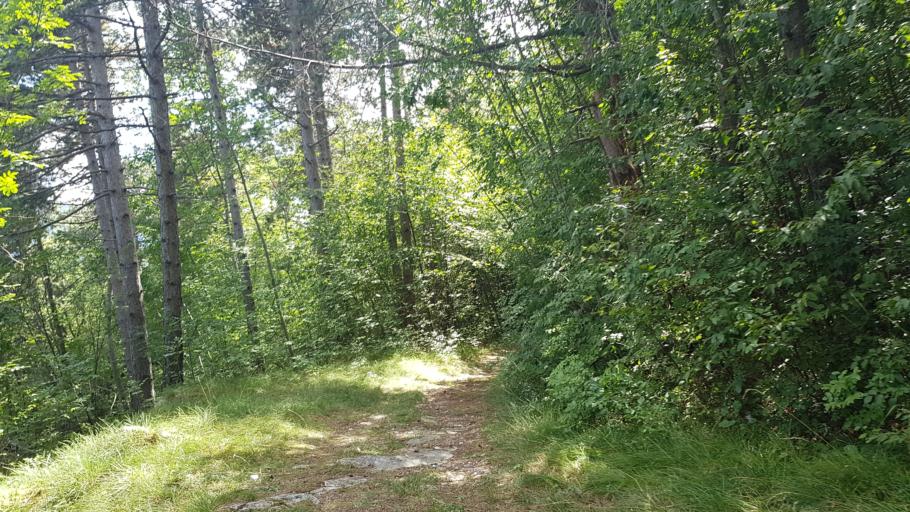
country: IT
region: Trentino-Alto Adige
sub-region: Provincia di Trento
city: Vezzano
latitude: 46.0897
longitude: 11.0014
